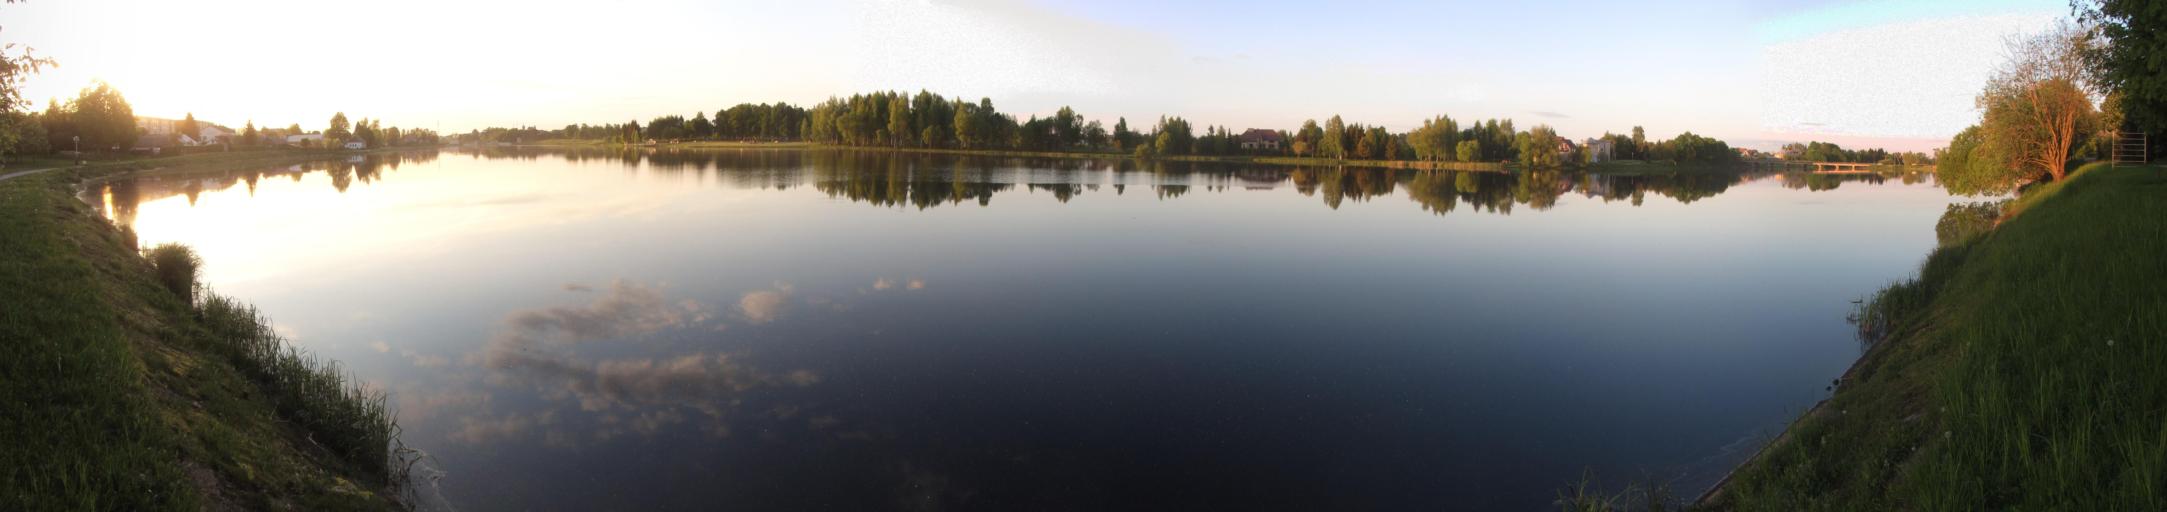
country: LT
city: Sirvintos
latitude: 55.0398
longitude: 24.9613
